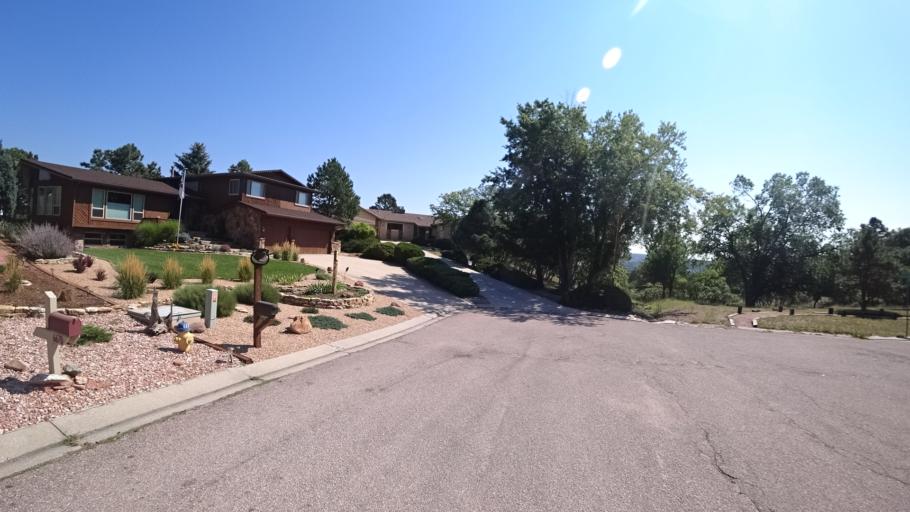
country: US
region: Colorado
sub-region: El Paso County
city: Air Force Academy
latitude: 38.9283
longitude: -104.8274
